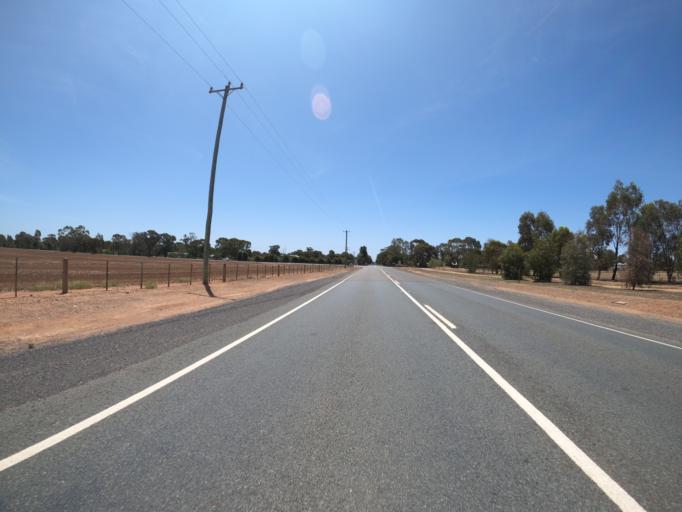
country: AU
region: Victoria
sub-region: Moira
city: Yarrawonga
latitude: -36.0420
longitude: 145.9955
